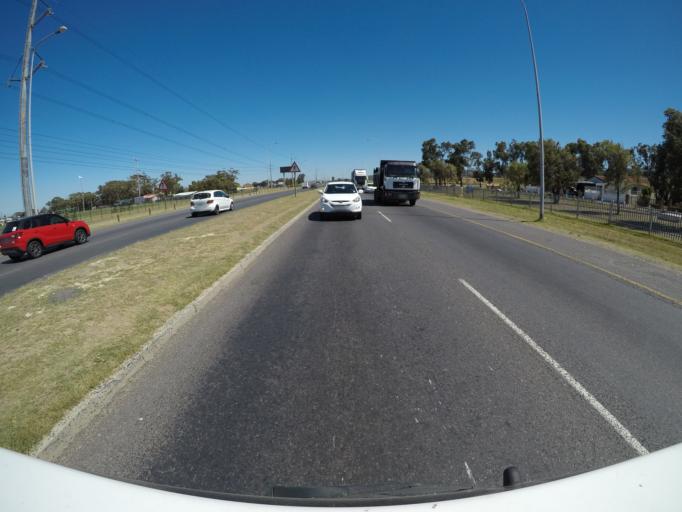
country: ZA
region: Western Cape
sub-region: Cape Winelands District Municipality
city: Stellenbosch
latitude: -34.0875
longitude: 18.8376
